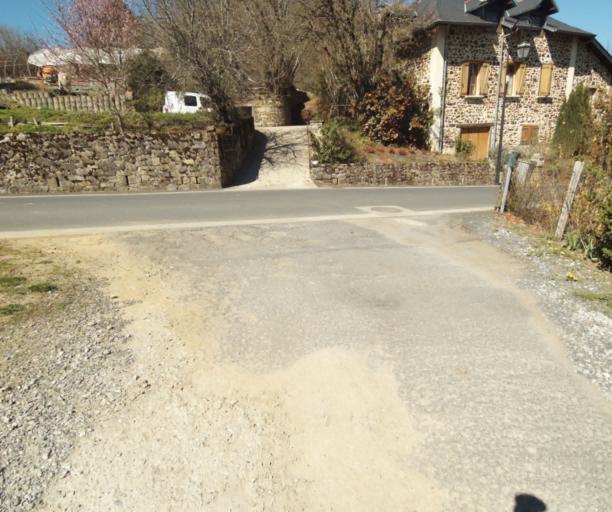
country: FR
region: Limousin
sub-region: Departement de la Correze
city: Chamboulive
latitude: 45.3987
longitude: 1.6454
